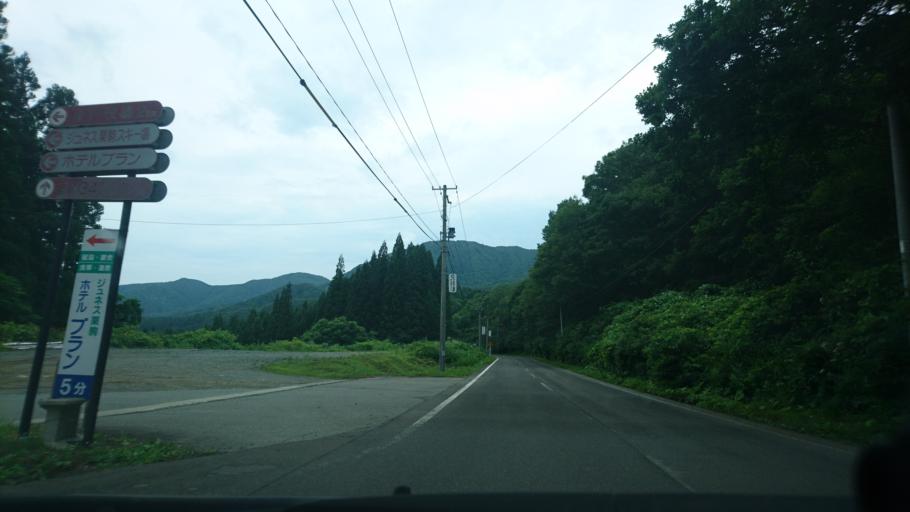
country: JP
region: Akita
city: Yokotemachi
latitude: 39.1723
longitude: 140.7336
